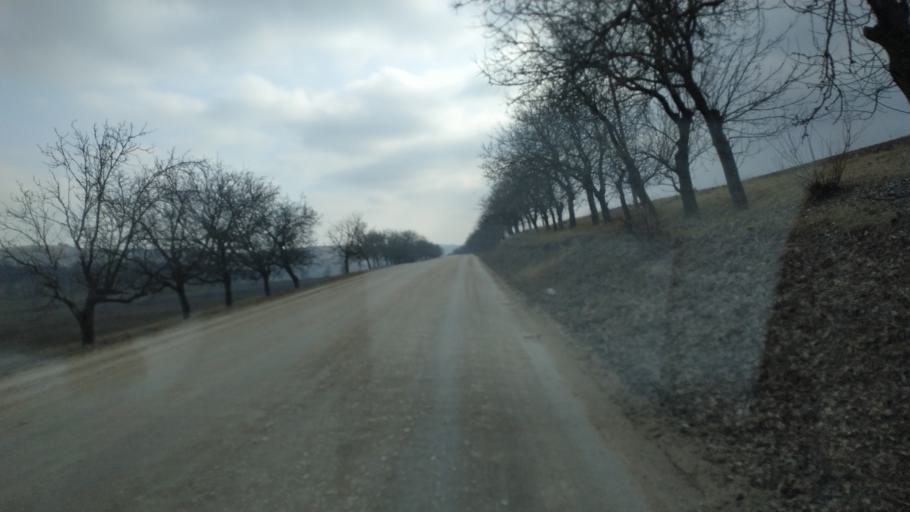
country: MD
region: Hincesti
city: Dancu
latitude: 46.9248
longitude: 28.3281
